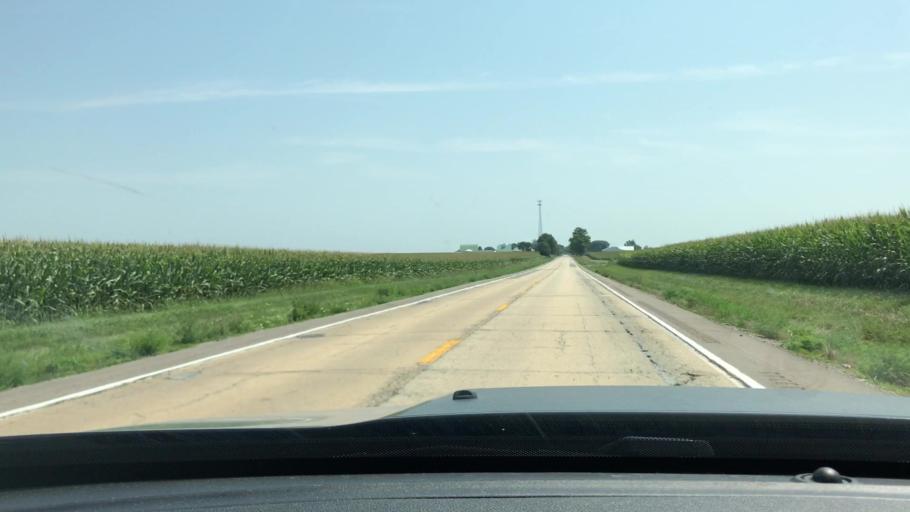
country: US
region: Illinois
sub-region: LaSalle County
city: Earlville
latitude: 41.4690
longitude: -88.9514
